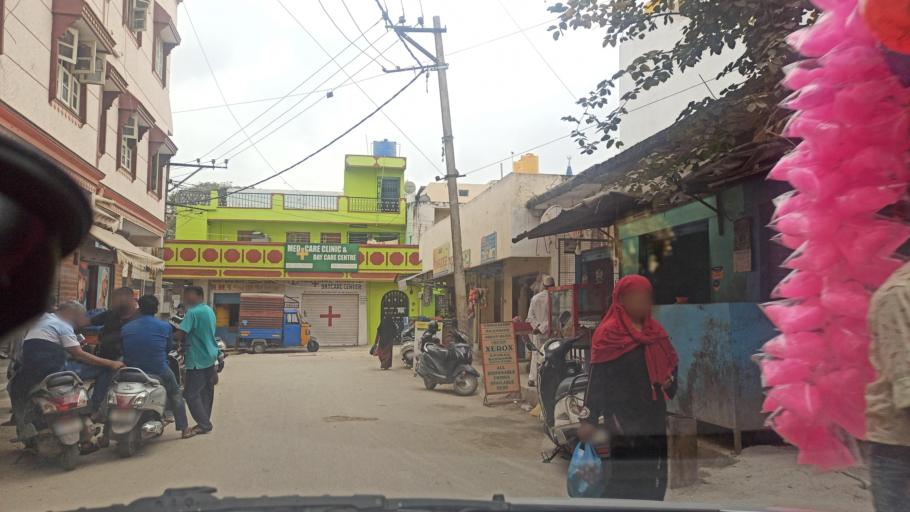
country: IN
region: Karnataka
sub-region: Bangalore Urban
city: Bangalore
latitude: 13.0349
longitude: 77.6217
